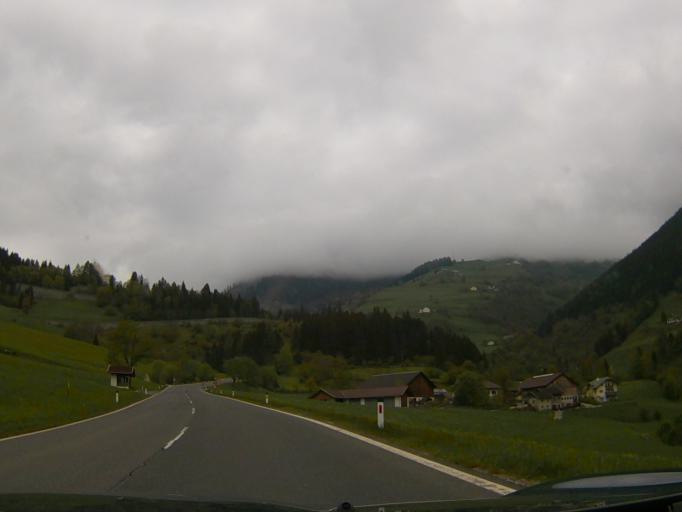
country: AT
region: Carinthia
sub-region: Politischer Bezirk Spittal an der Drau
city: Obervellach
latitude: 46.9619
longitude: 13.1853
